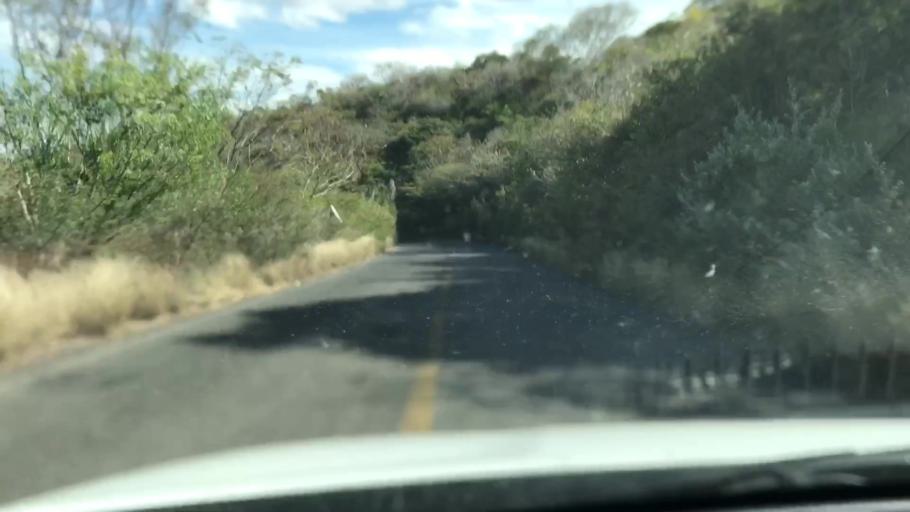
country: MX
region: Jalisco
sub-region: Zacoalco de Torres
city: Barranca de Otates (Barranca de Otatan)
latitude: 20.2571
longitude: -103.6751
